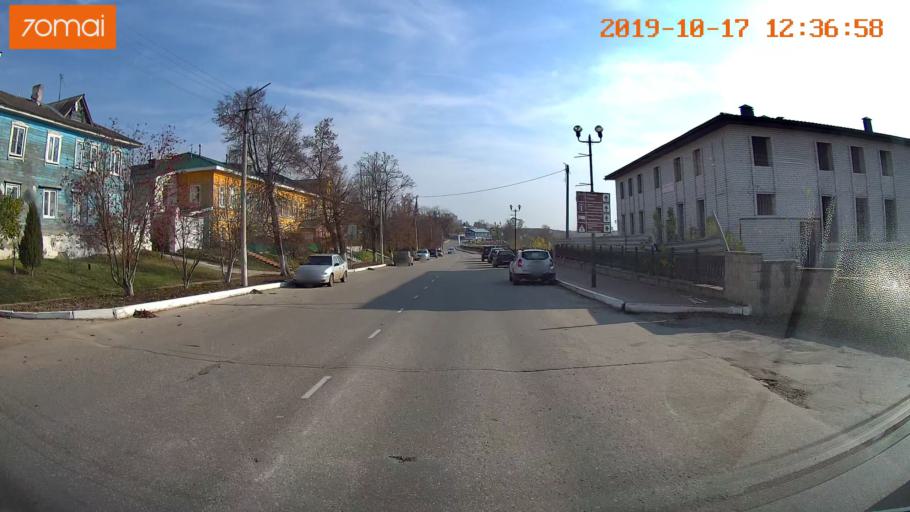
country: RU
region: Rjazan
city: Kasimov
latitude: 54.9381
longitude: 41.3816
